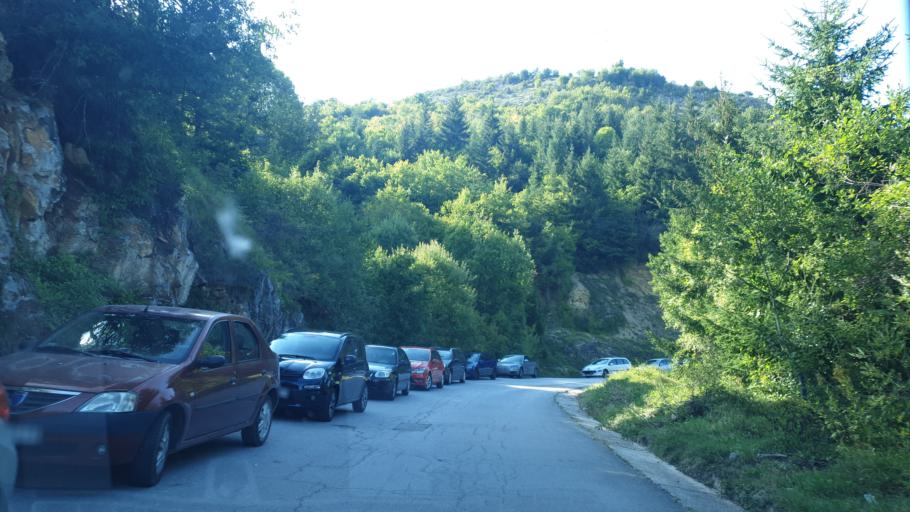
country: RS
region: Central Serbia
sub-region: Zlatiborski Okrug
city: Nova Varos
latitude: 43.4190
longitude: 19.9245
